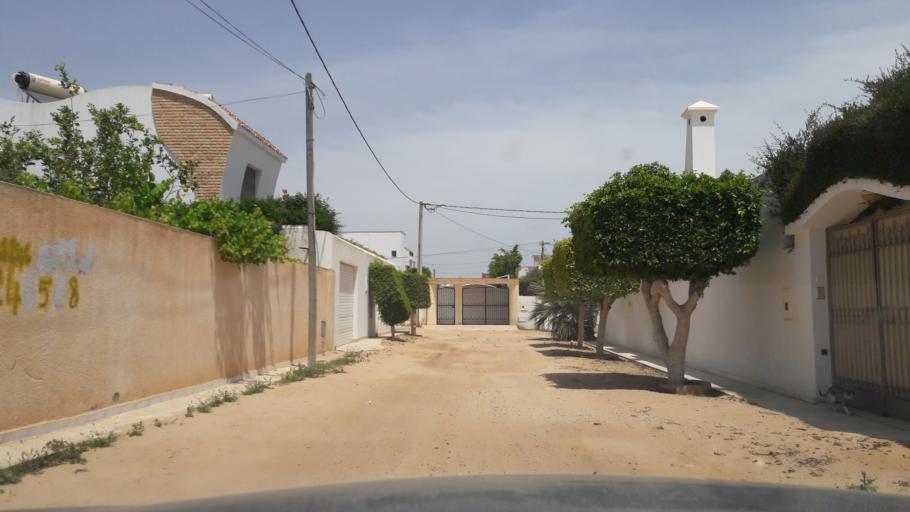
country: TN
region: Safaqis
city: Sfax
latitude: 34.7786
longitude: 10.7564
